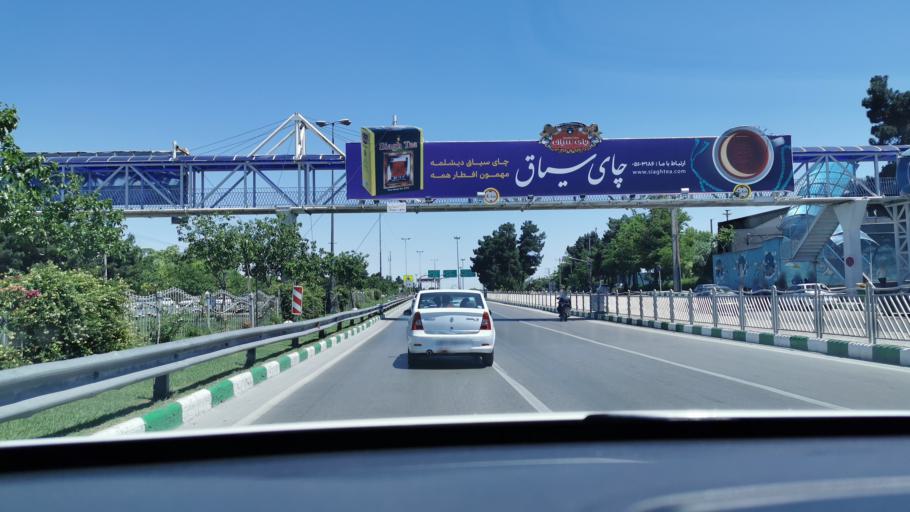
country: IR
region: Razavi Khorasan
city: Mashhad
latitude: 36.2541
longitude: 59.6027
